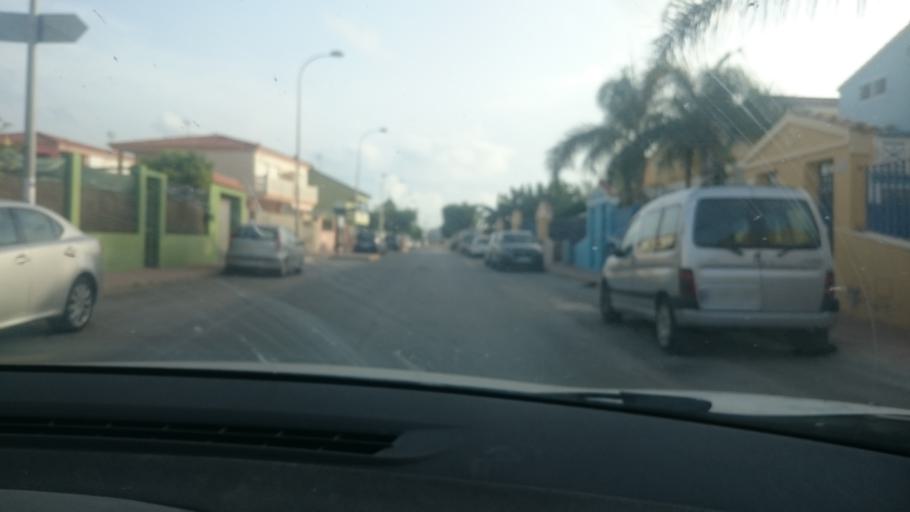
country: ES
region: Valencia
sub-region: Provincia de Castello
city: Moncofar
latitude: 39.7803
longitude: -0.1477
